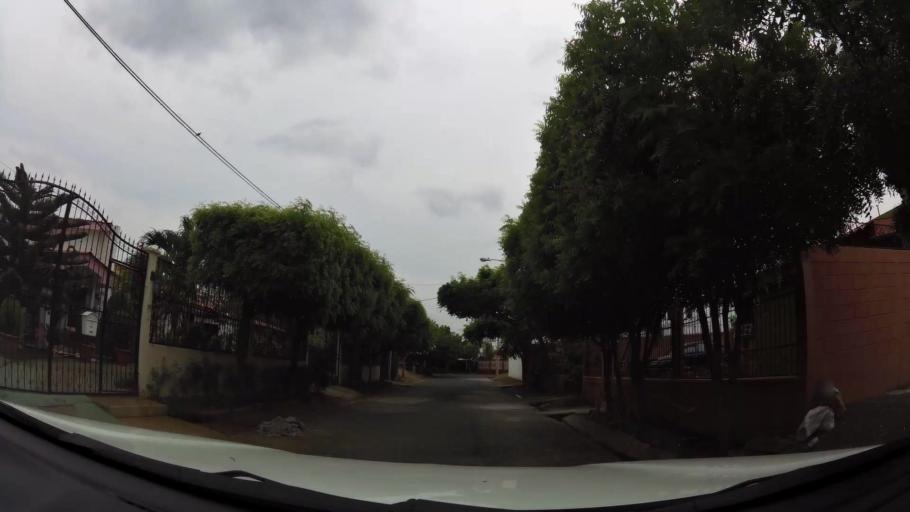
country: NI
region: Masaya
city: Ticuantepe
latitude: 12.0744
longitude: -86.1737
